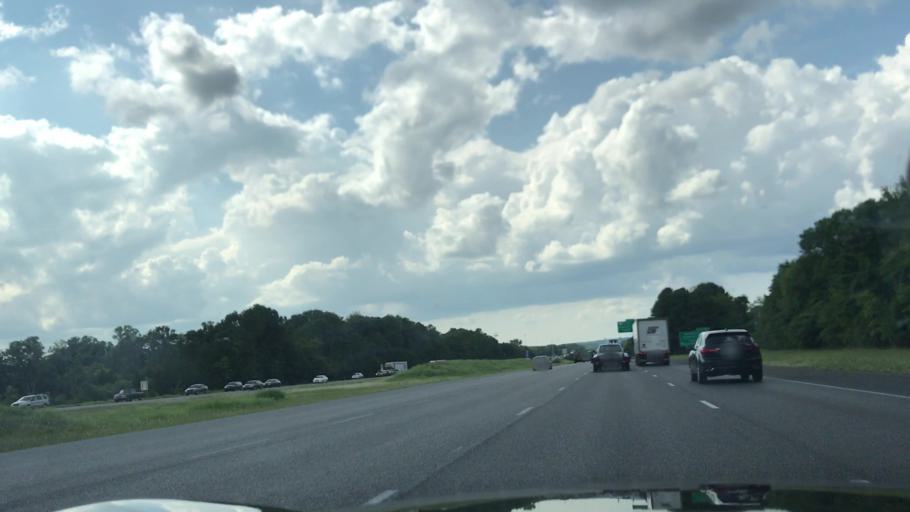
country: US
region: Tennessee
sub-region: Rutherford County
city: Smyrna
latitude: 35.9263
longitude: -86.5222
